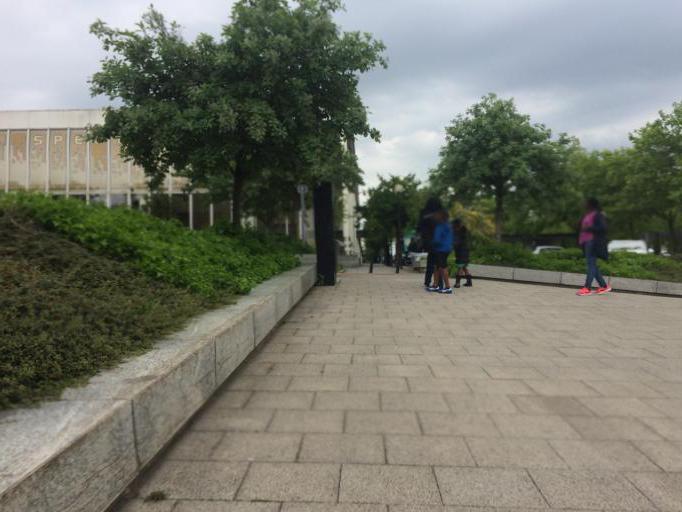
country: GB
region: England
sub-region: Milton Keynes
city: Milton Keynes
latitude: 52.0416
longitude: -0.7523
